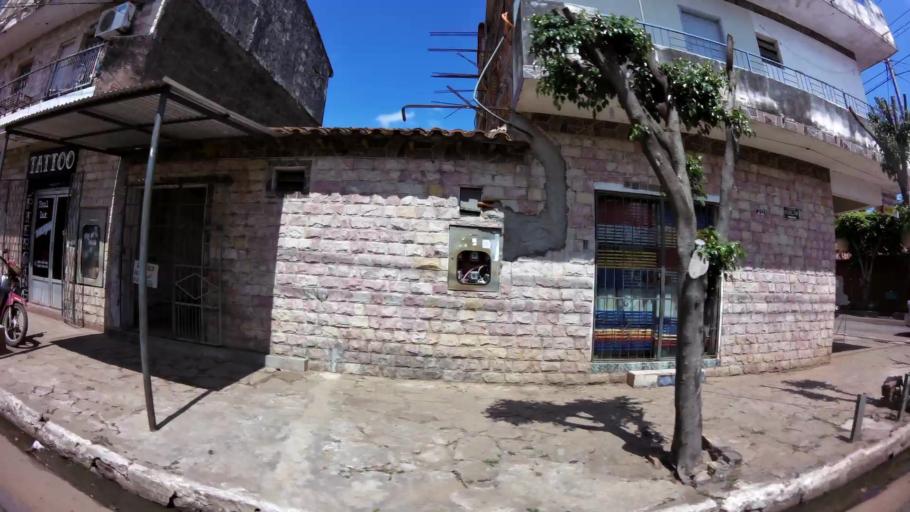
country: PY
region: Central
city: Fernando de la Mora
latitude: -25.3271
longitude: -57.5609
